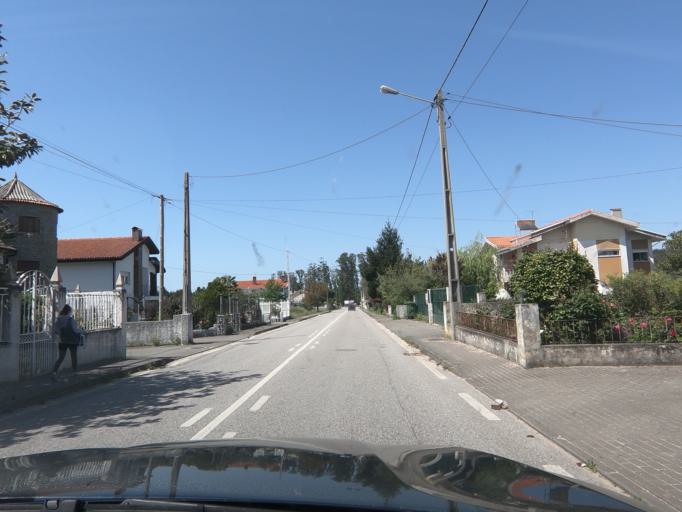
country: PT
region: Coimbra
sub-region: Lousa
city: Lousa
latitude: 40.1332
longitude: -8.2501
